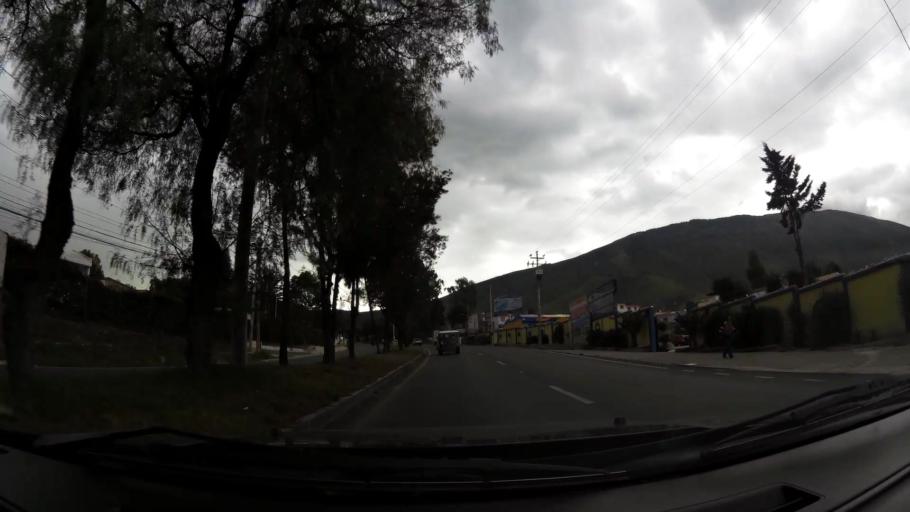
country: EC
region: Pichincha
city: Quito
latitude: -0.0657
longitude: -78.4623
